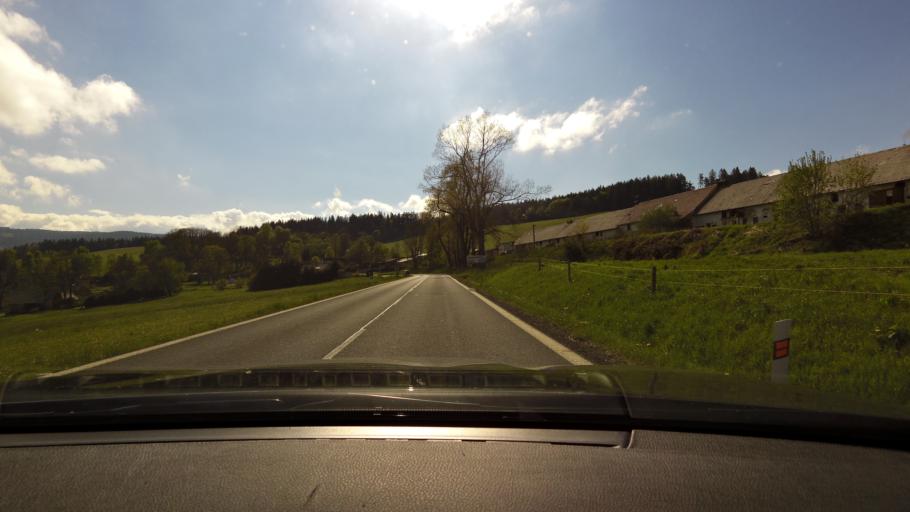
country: CZ
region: Plzensky
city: Strazov
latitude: 49.2480
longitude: 13.2993
